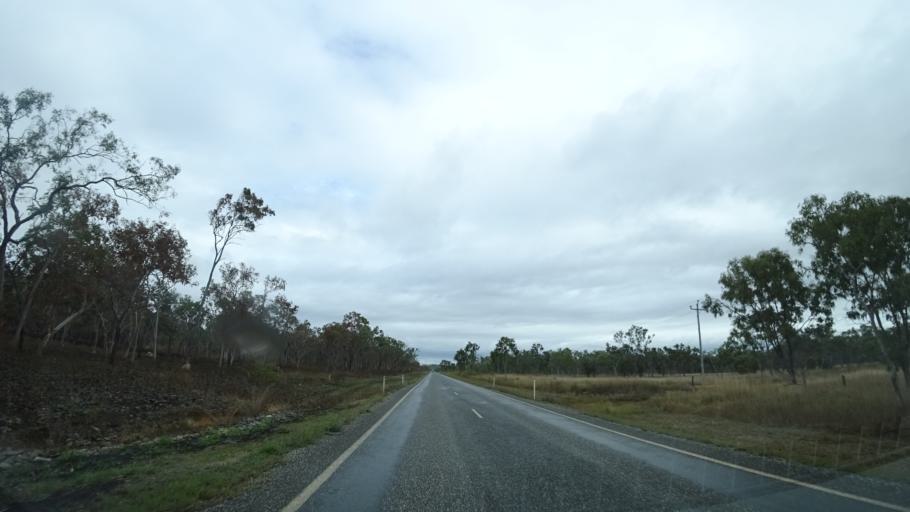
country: AU
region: Queensland
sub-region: Tablelands
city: Mareeba
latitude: -16.7551
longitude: 145.3427
